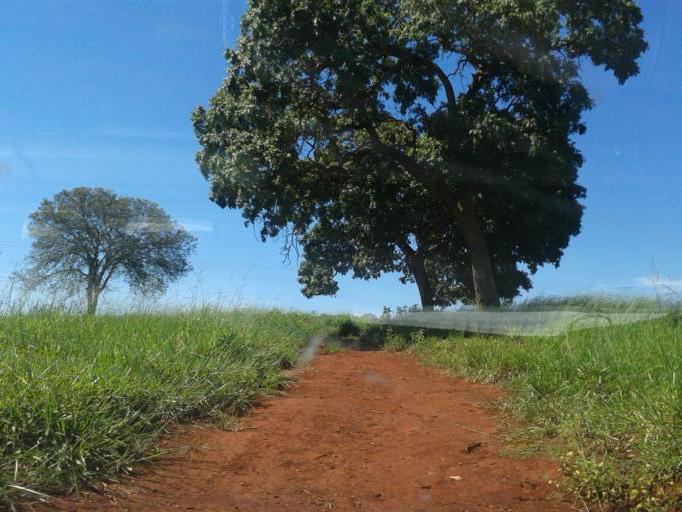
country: BR
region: Minas Gerais
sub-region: Capinopolis
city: Capinopolis
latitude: -18.6326
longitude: -49.6102
